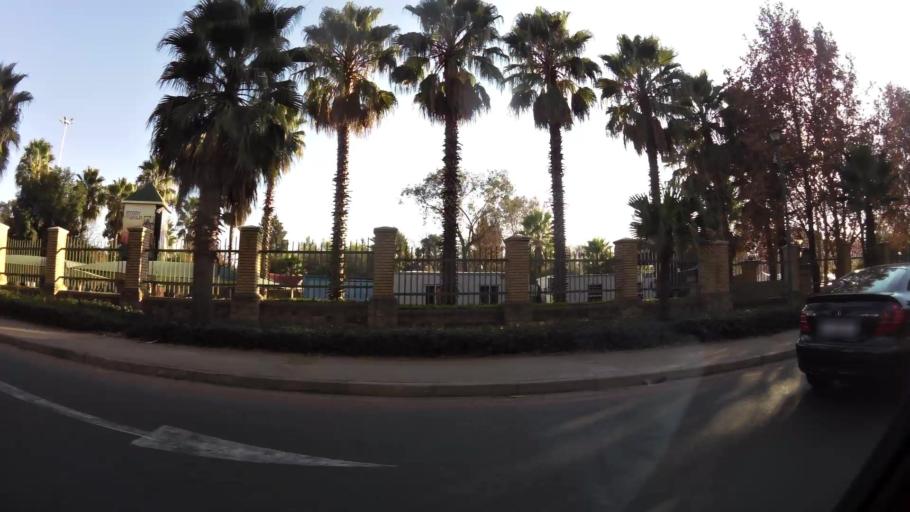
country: ZA
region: Gauteng
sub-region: City of Johannesburg Metropolitan Municipality
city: Johannesburg
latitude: -26.2374
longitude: 28.0118
